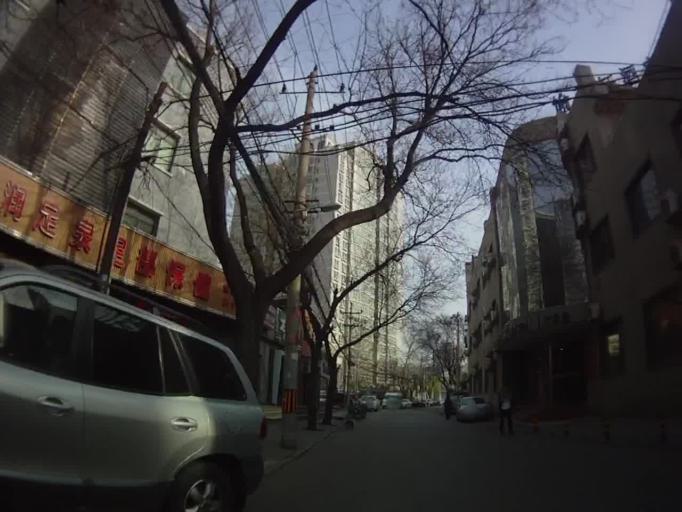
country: CN
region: Beijing
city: Chaowai
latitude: 39.9036
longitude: 116.4415
